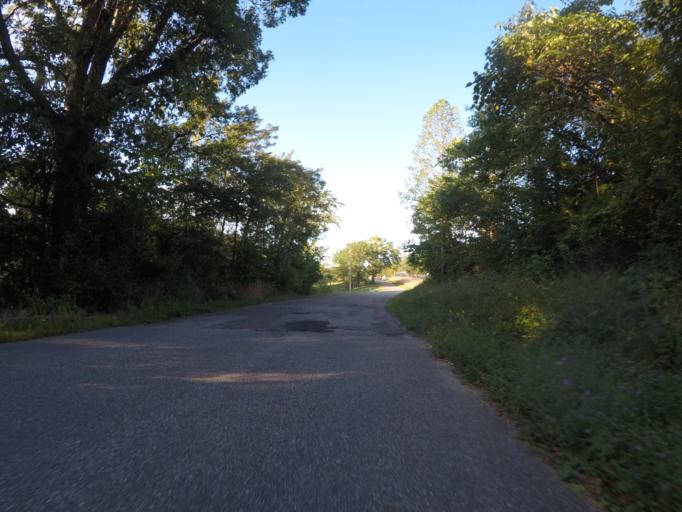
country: US
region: Ohio
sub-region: Lawrence County
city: Coal Grove
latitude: 38.5881
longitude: -82.5518
